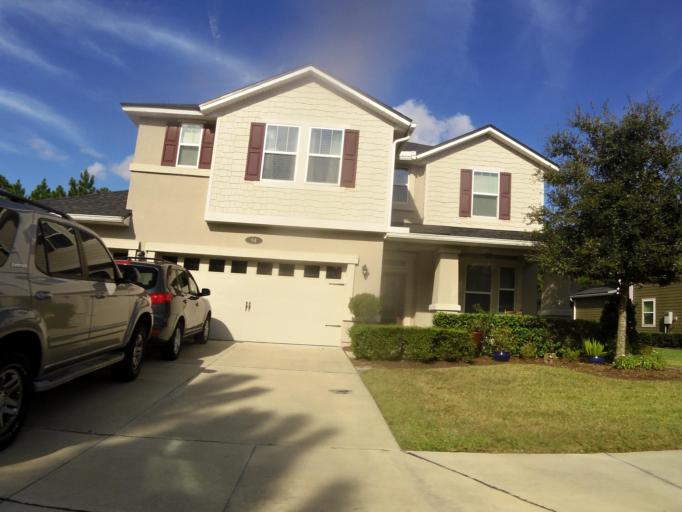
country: US
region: Florida
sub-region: Clay County
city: Green Cove Springs
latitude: 29.9332
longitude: -81.5169
